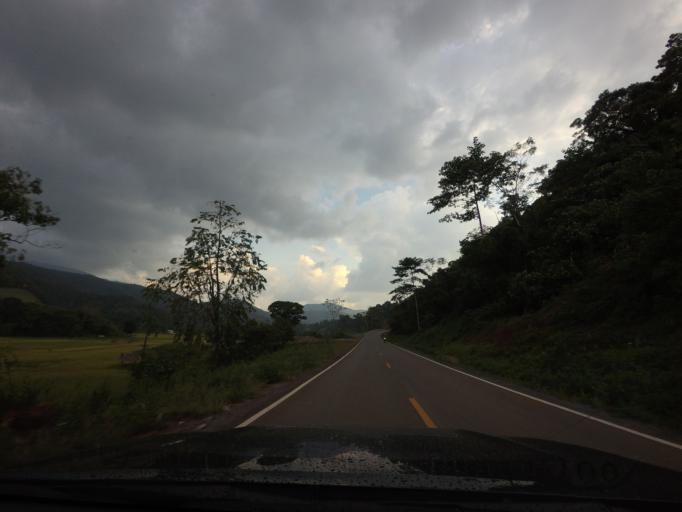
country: TH
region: Nan
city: Bo Kluea
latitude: 19.2269
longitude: 101.1826
